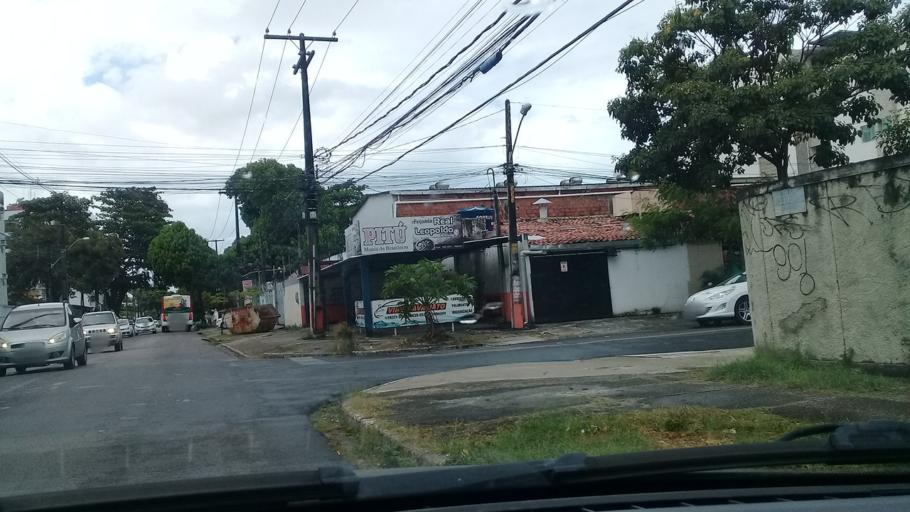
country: BR
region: Pernambuco
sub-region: Recife
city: Recife
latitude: -8.1380
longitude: -34.9143
